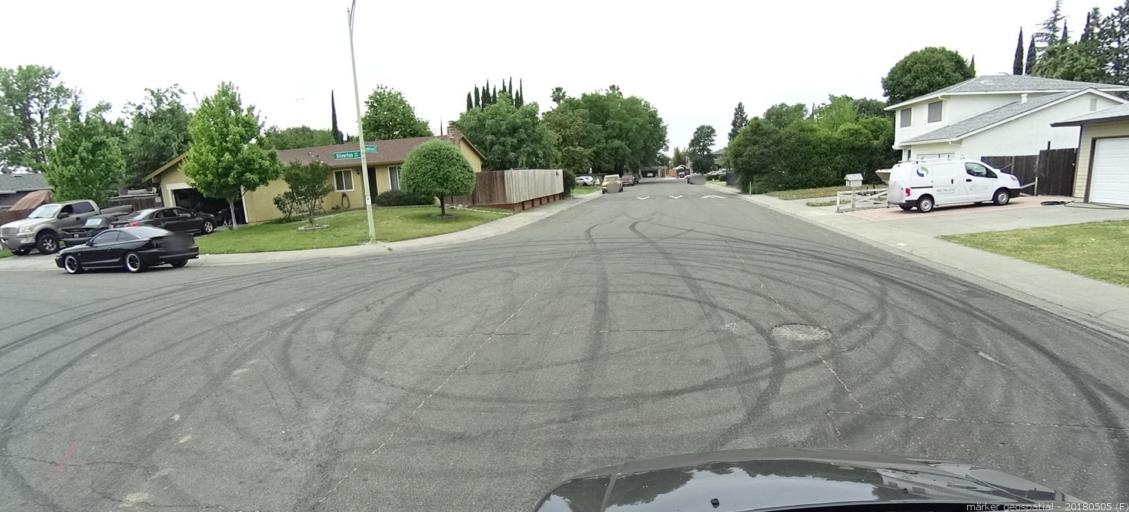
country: US
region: California
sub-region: Sacramento County
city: Rio Linda
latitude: 38.6507
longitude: -121.4674
